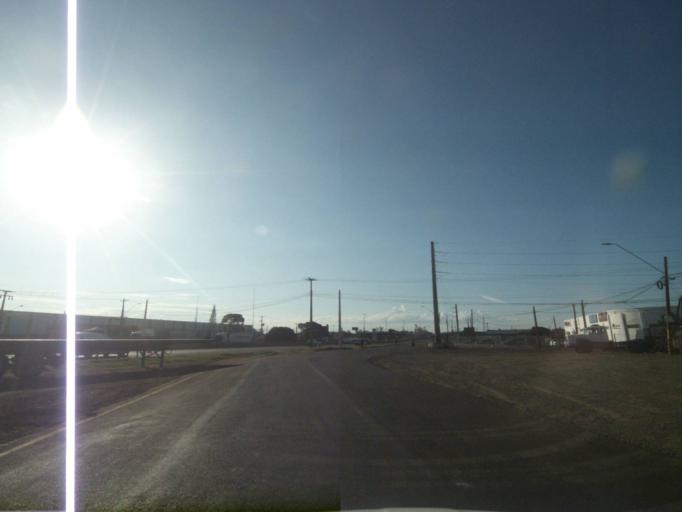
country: BR
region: Parana
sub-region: Cambe
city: Cambe
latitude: -23.2980
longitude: -51.2298
